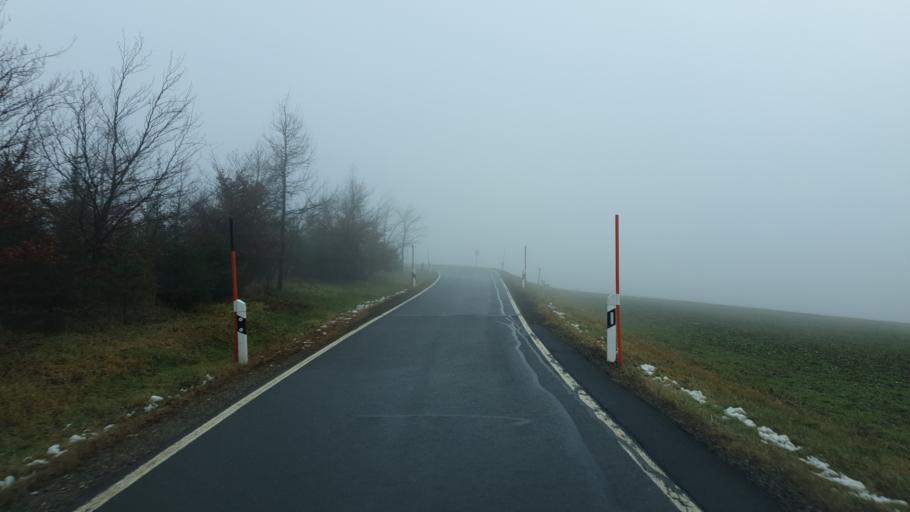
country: DE
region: Saxony
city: Neuhausen
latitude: 50.6594
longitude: 13.4692
